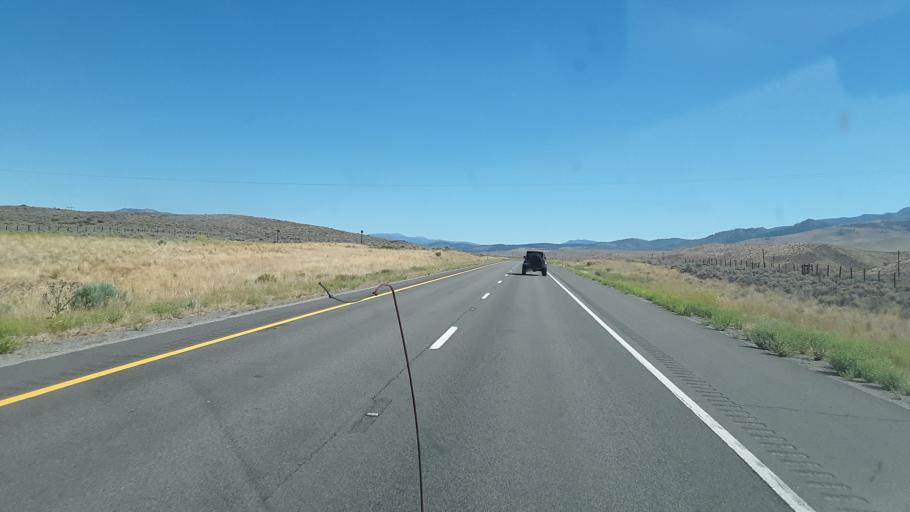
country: US
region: Nevada
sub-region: Washoe County
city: Cold Springs
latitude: 39.7240
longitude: -120.0386
